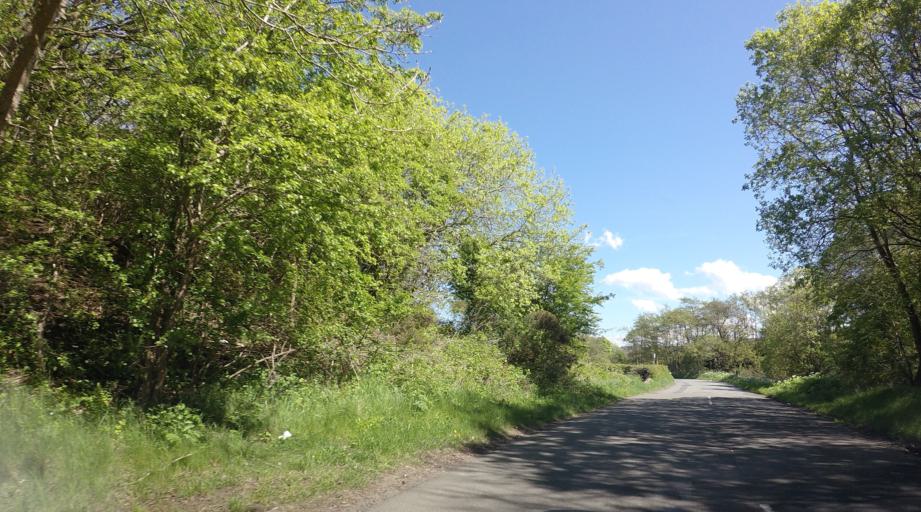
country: GB
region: Scotland
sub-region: Falkirk
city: Polmont
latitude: 55.9729
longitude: -3.6647
